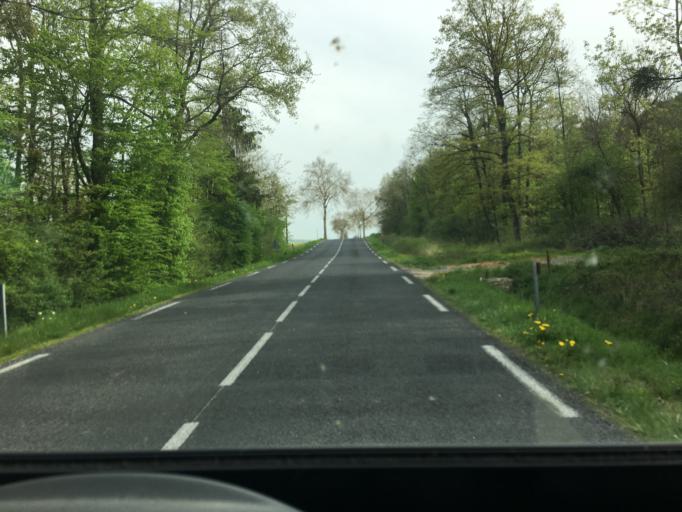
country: FR
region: Lorraine
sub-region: Departement de Meurthe-et-Moselle
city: Einville-au-Jard
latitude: 48.7040
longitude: 6.5074
